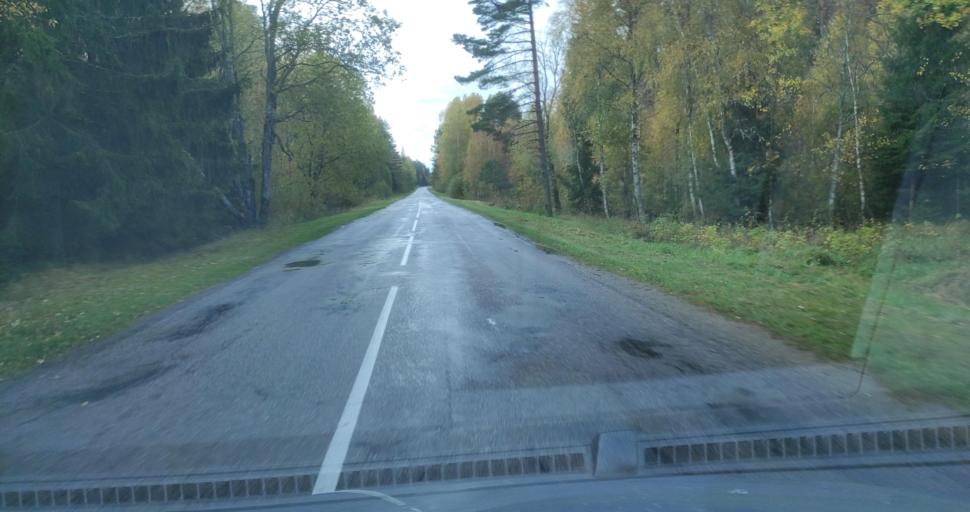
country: LV
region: Skrunda
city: Skrunda
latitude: 56.6601
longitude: 22.0222
